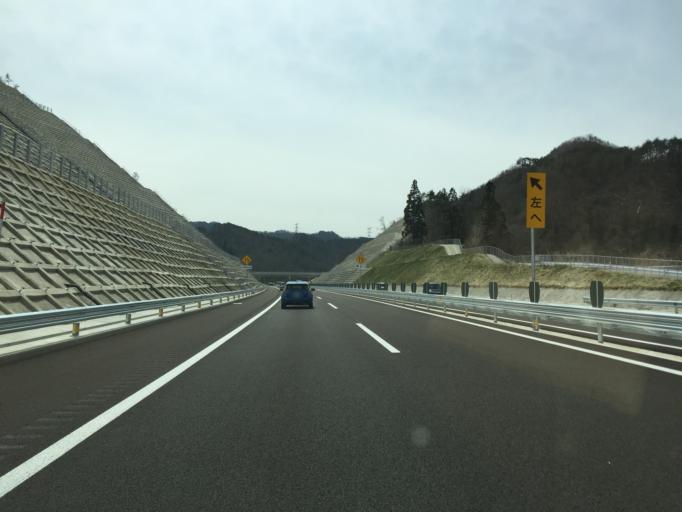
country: JP
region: Yamagata
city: Kaminoyama
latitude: 38.1216
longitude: 140.2507
